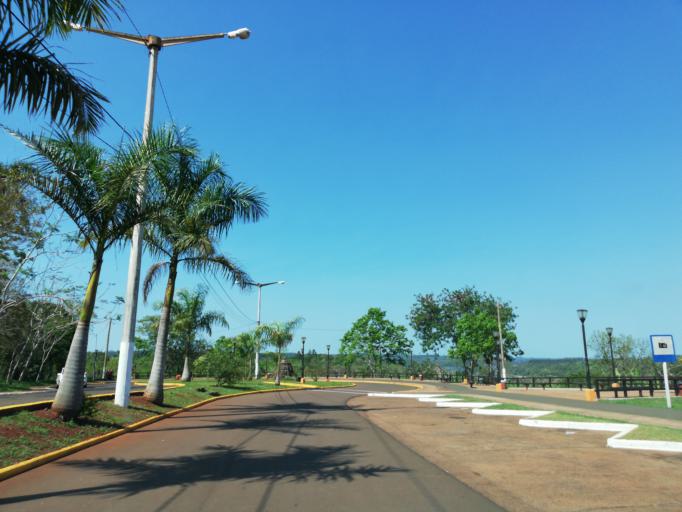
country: AR
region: Misiones
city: Puerto Eldorado
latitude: -26.4152
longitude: -54.6933
